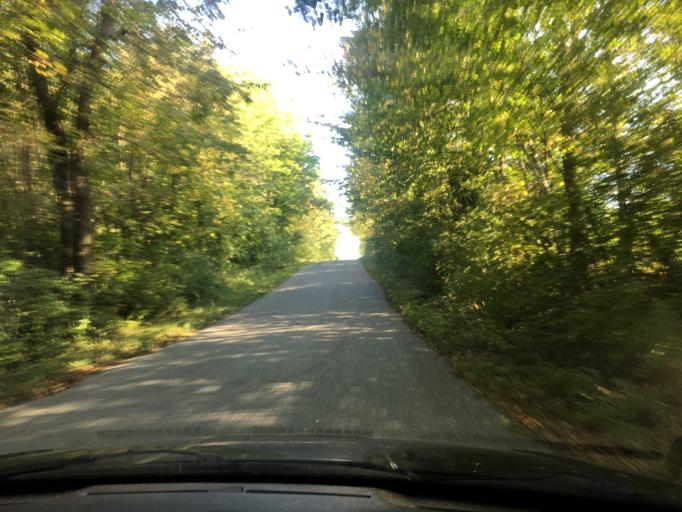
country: US
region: Ohio
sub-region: Logan County
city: West Liberty
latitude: 40.2545
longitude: -83.6627
